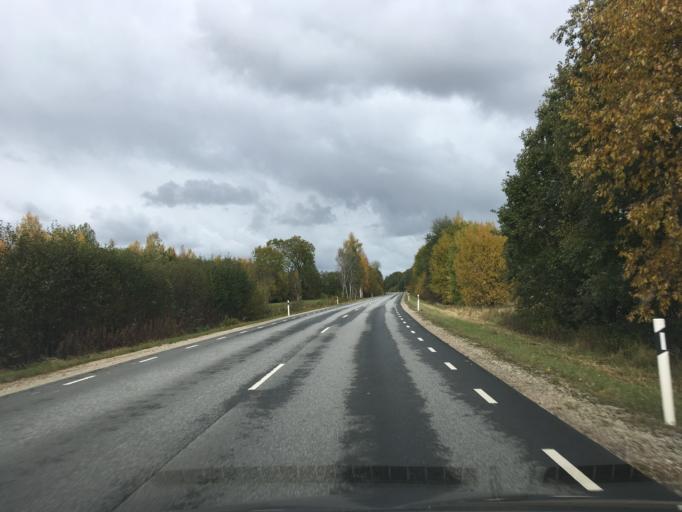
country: EE
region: Harju
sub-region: Anija vald
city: Kehra
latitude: 59.3010
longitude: 25.3602
